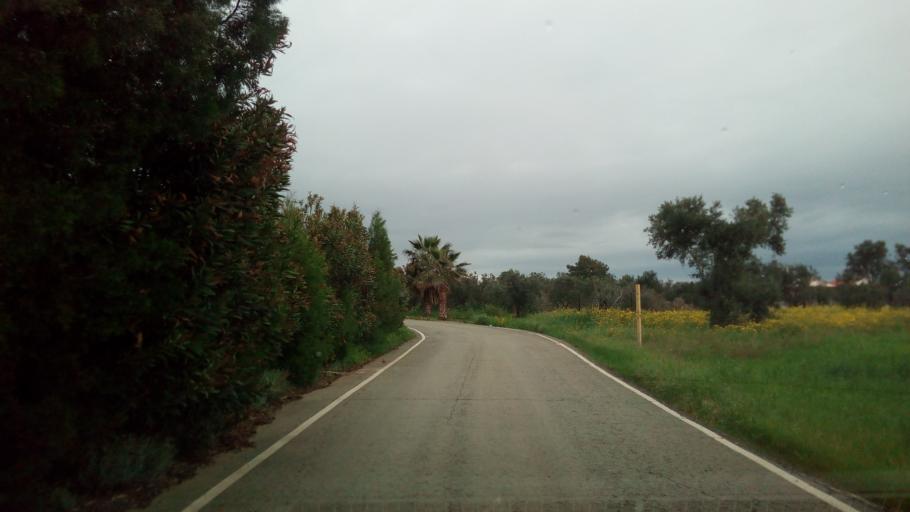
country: CY
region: Larnaka
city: Kofinou
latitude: 34.8704
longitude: 33.4493
